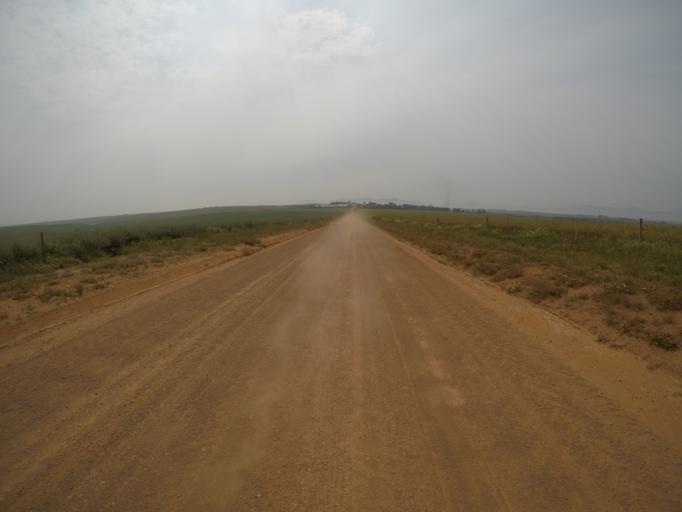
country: ZA
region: Western Cape
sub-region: City of Cape Town
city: Kraaifontein
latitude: -33.7136
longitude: 18.6847
